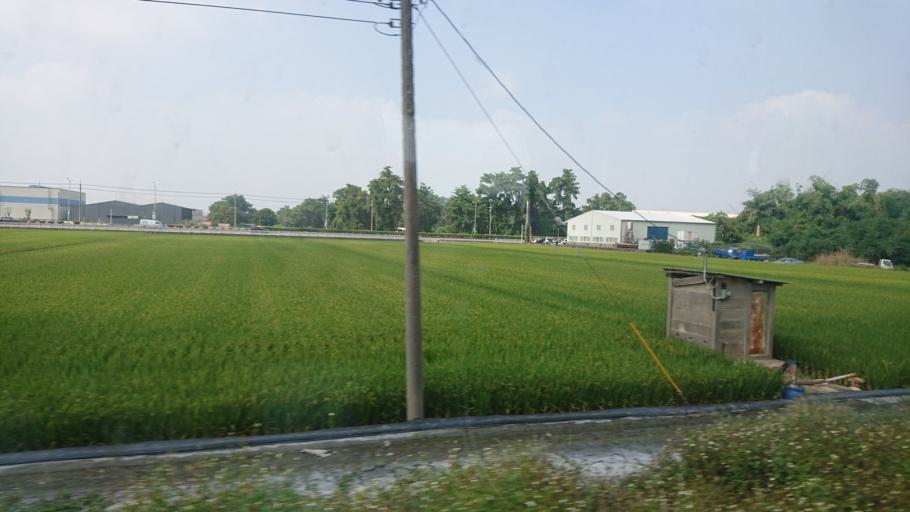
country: TW
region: Taiwan
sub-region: Yunlin
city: Douliu
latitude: 23.6367
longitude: 120.4704
